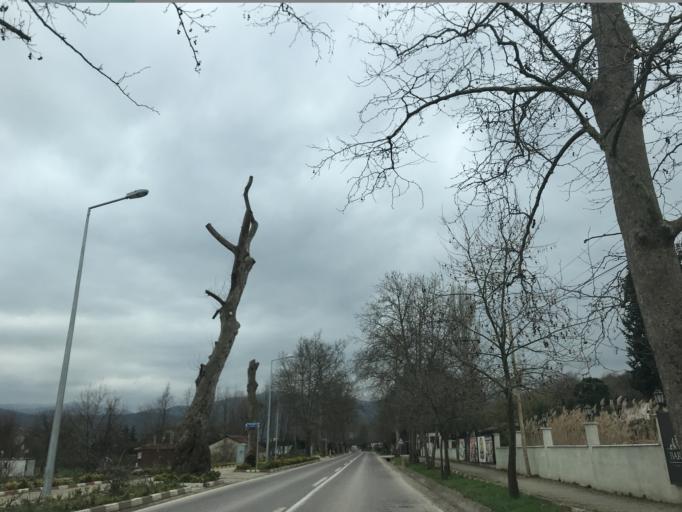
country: TR
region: Yalova
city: Kadikoy
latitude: 40.6253
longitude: 29.2212
